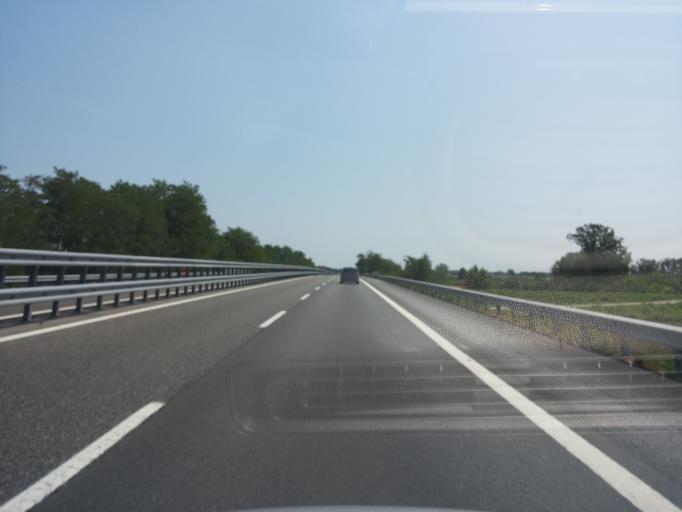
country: IT
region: Emilia-Romagna
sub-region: Provincia di Piacenza
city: Sarmato
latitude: 45.0695
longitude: 9.5012
